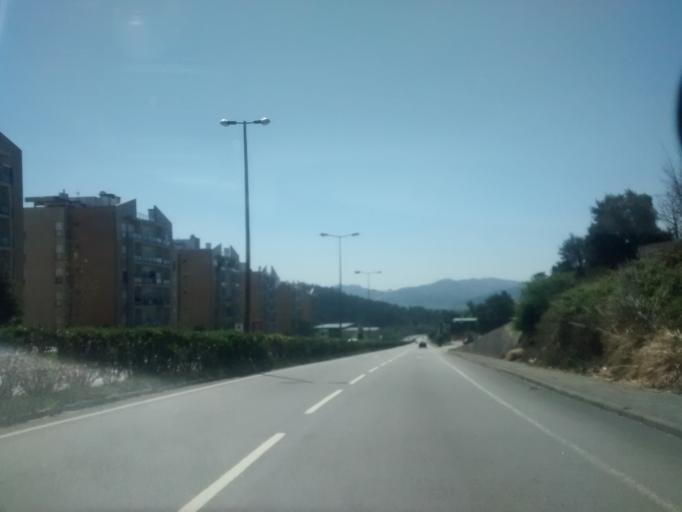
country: PT
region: Braga
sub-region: Braga
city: Braga
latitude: 41.5319
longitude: -8.4120
